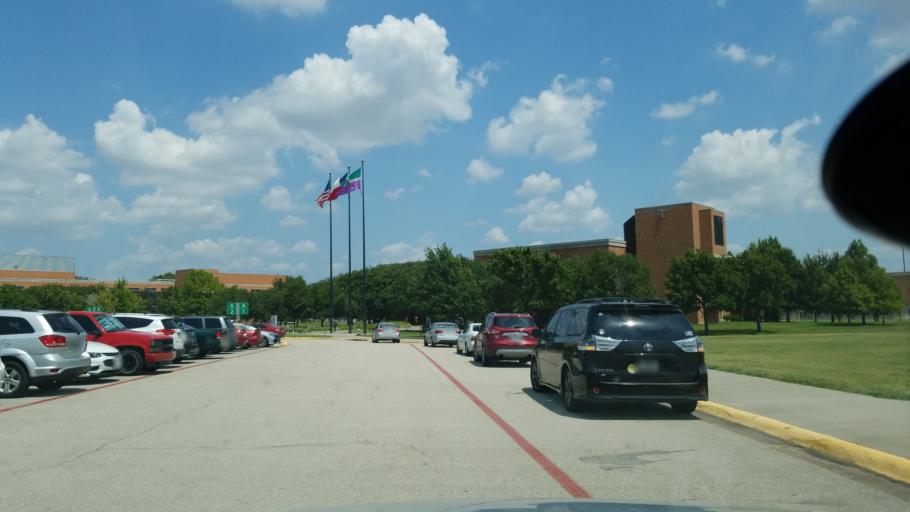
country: US
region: Texas
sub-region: Dallas County
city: Richardson
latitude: 32.9200
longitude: -96.7319
